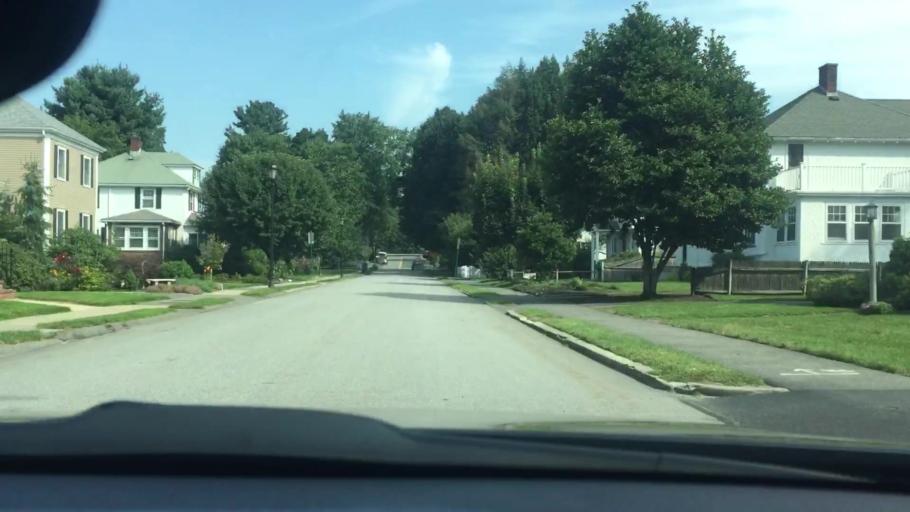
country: US
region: Massachusetts
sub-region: Norfolk County
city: Wellesley
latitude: 42.3048
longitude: -71.2801
